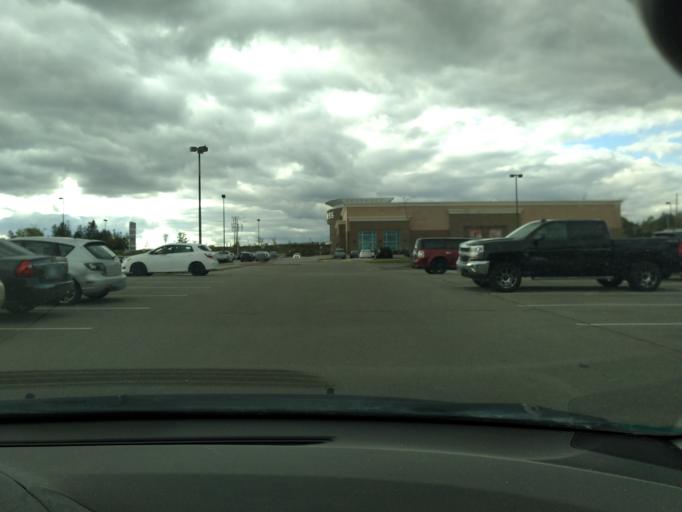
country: CA
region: Ontario
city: Newmarket
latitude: 44.0766
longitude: -79.4829
